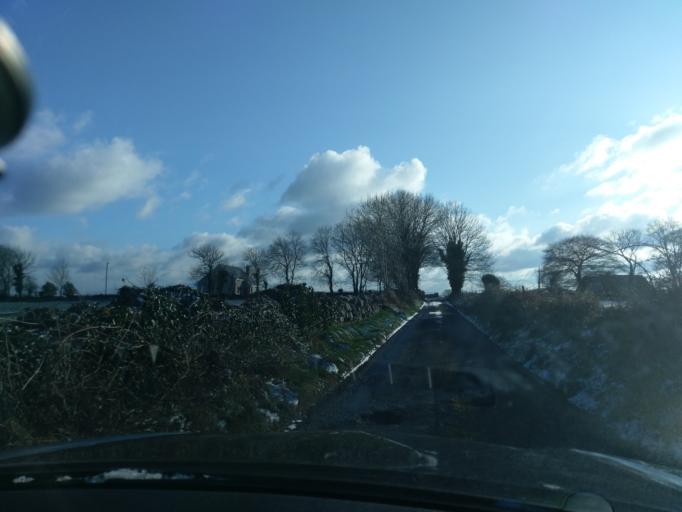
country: IE
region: Connaught
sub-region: County Galway
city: Gort
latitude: 53.1724
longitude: -8.7945
